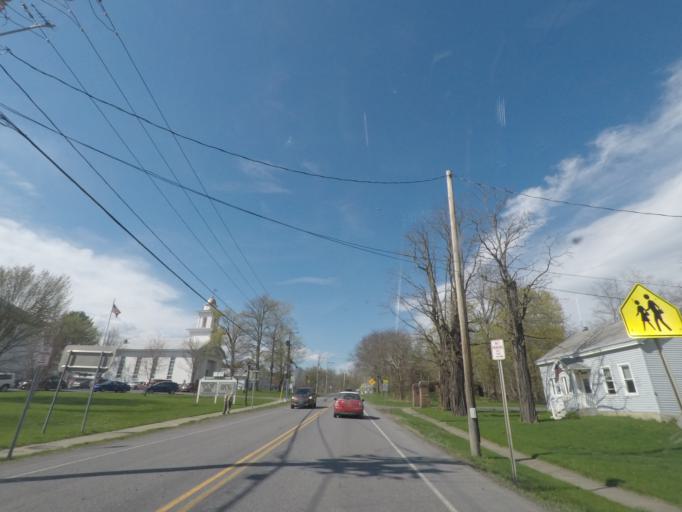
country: US
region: New York
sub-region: Greene County
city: Cairo
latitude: 42.4160
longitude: -74.0222
